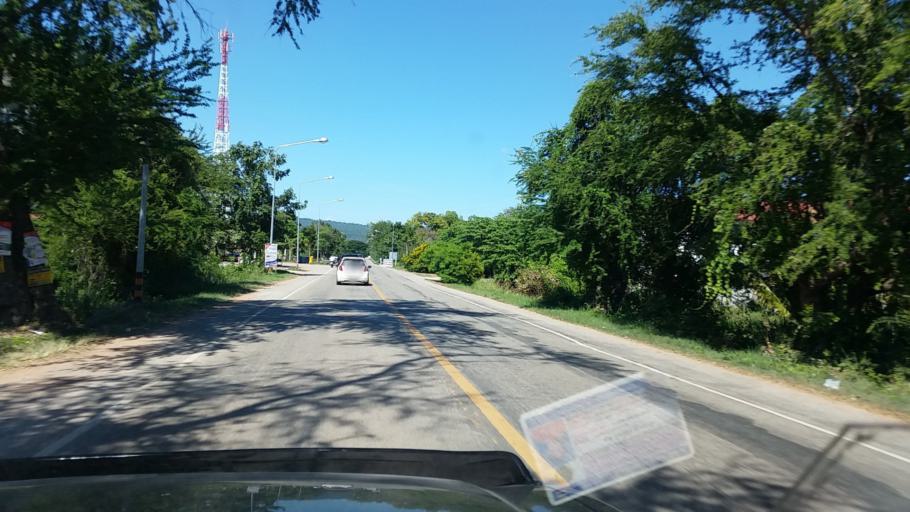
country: TH
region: Chaiyaphum
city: Chaiyaphum
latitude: 15.9375
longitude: 102.0230
